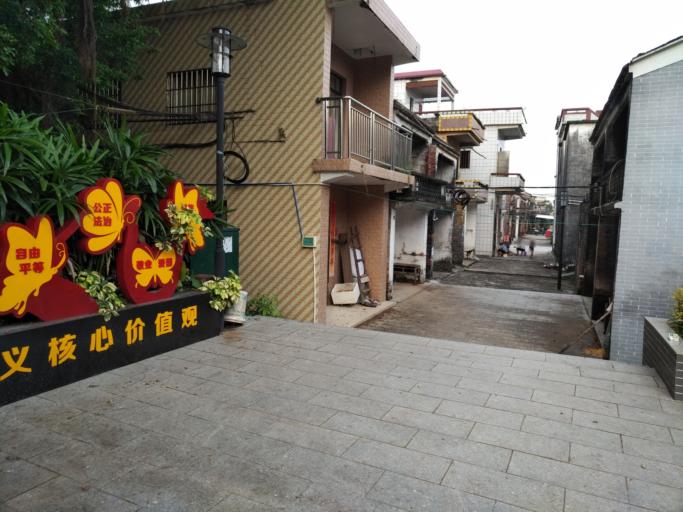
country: CN
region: Guangdong
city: Da'ao
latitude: 22.4547
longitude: 113.2092
